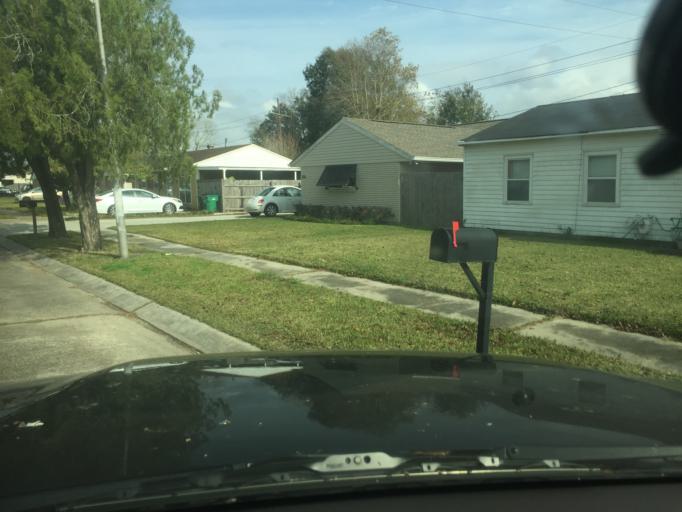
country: US
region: Louisiana
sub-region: Jefferson Parish
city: Avondale
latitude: 29.9132
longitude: -90.2000
